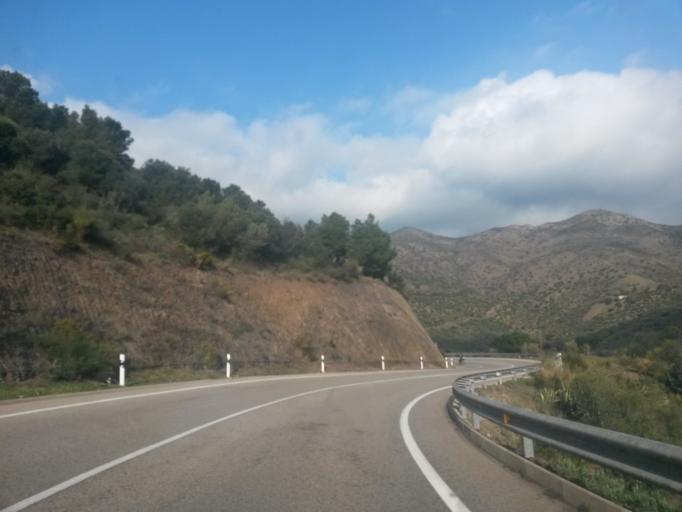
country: ES
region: Catalonia
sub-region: Provincia de Girona
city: Colera
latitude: 42.3998
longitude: 3.1490
